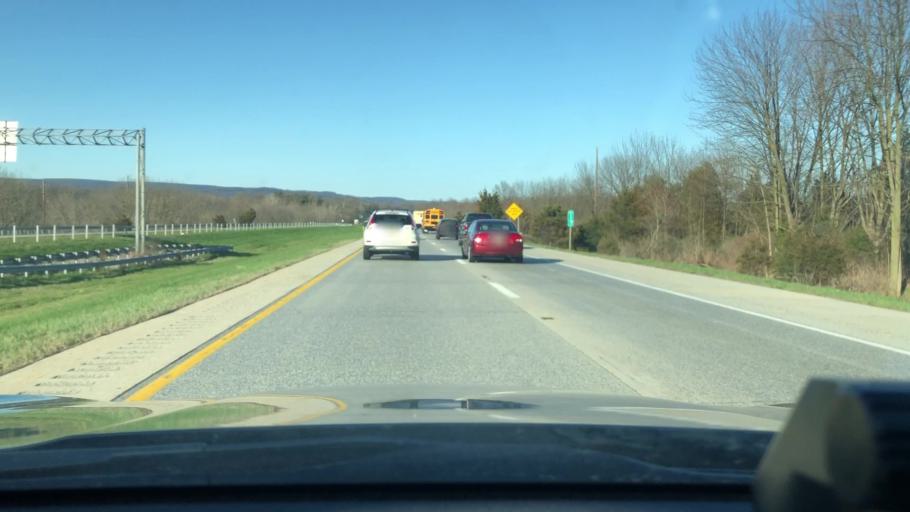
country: US
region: Pennsylvania
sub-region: Lebanon County
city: Jonestown
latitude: 40.4327
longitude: -76.4966
